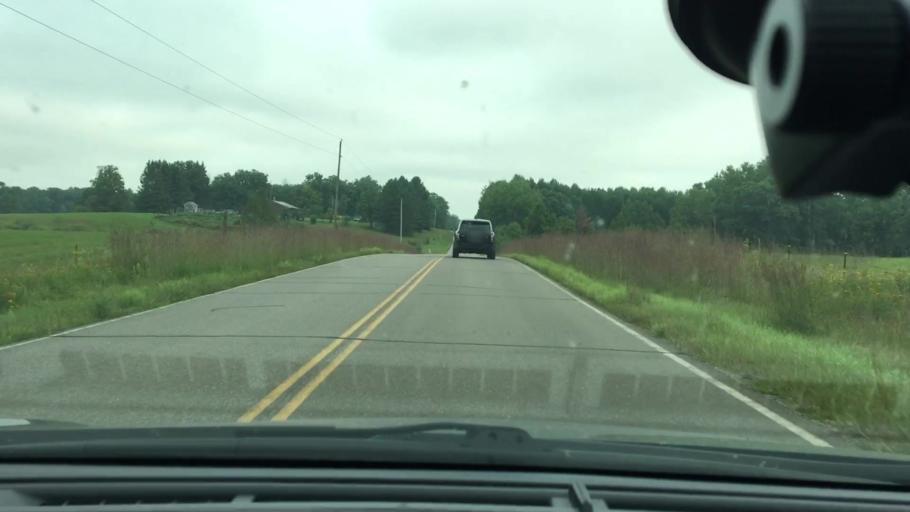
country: US
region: Minnesota
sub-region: Crow Wing County
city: Cross Lake
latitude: 46.6462
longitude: -94.0096
